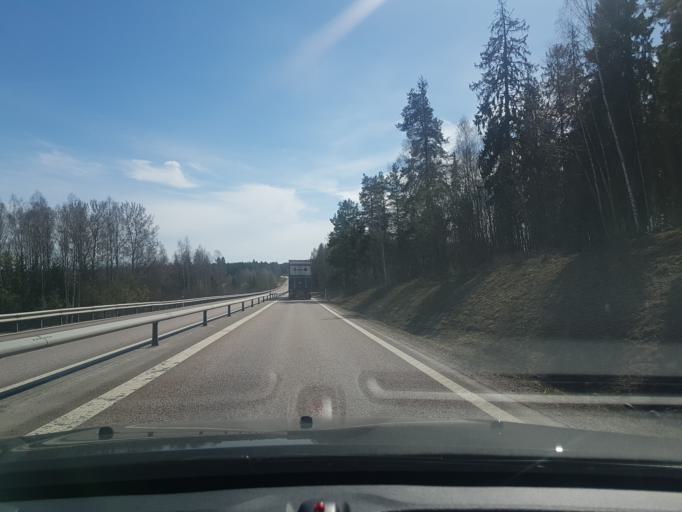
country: SE
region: Dalarna
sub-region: Hedemora Kommun
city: Brunna
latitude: 60.2379
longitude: 16.0302
